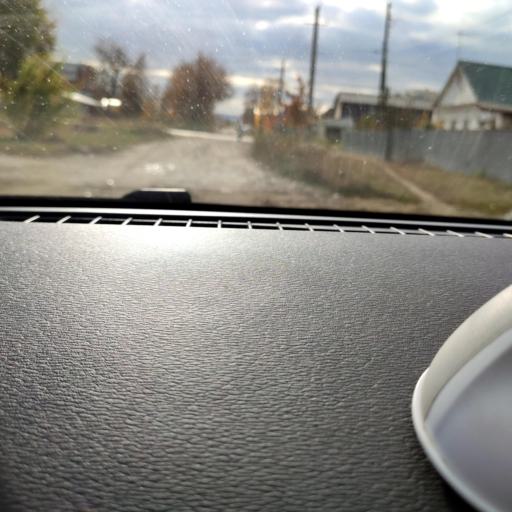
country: RU
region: Samara
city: Petra-Dubrava
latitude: 53.2465
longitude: 50.3140
